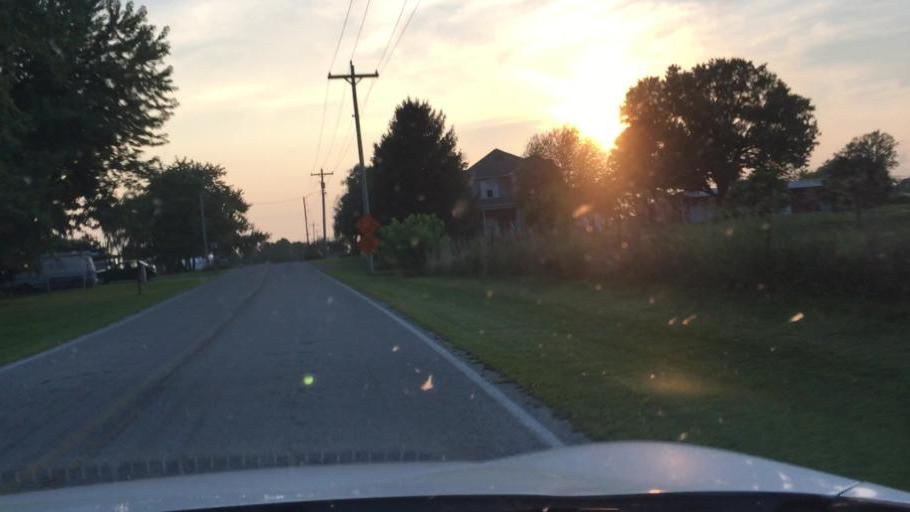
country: US
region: Ohio
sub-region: Madison County
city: Choctaw Lake
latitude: 39.9464
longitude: -83.5325
